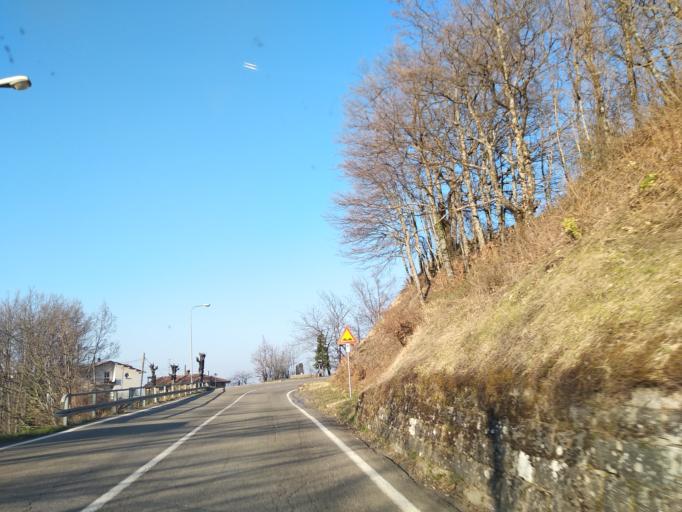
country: IT
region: Emilia-Romagna
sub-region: Provincia di Reggio Emilia
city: Ramiseto
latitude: 44.4152
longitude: 10.2863
